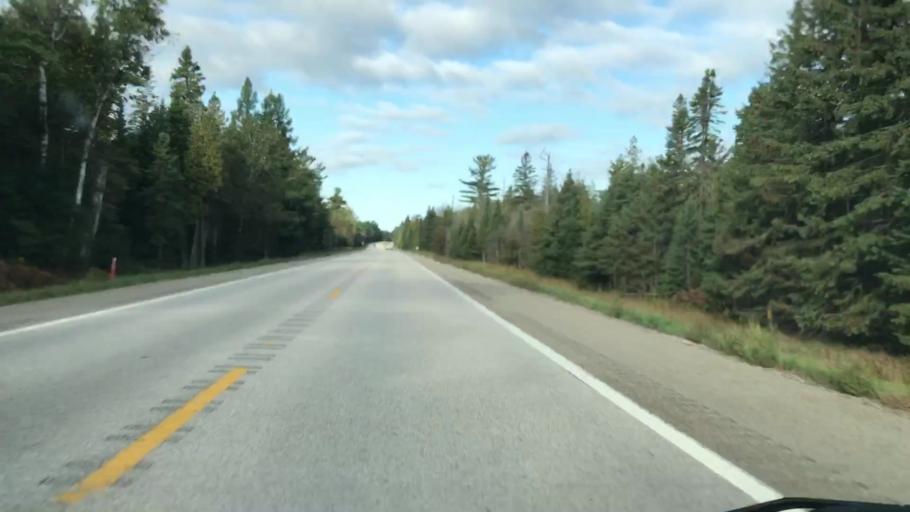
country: US
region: Michigan
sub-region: Luce County
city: Newberry
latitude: 46.3320
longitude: -85.0725
